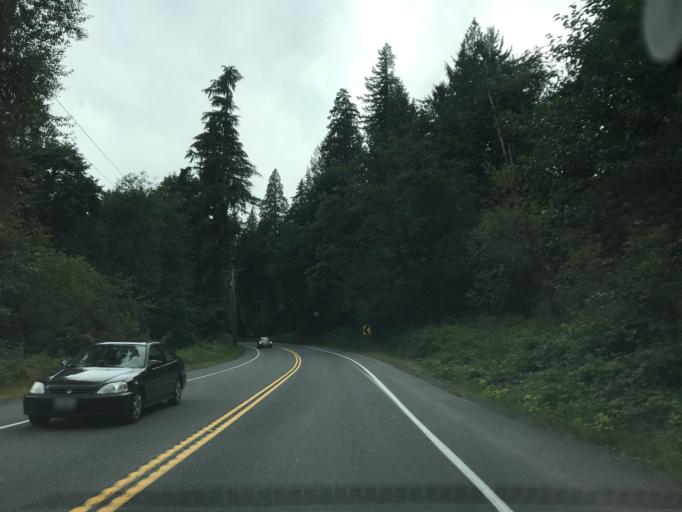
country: US
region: Washington
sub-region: King County
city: Fall City
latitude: 47.5326
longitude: -121.9181
